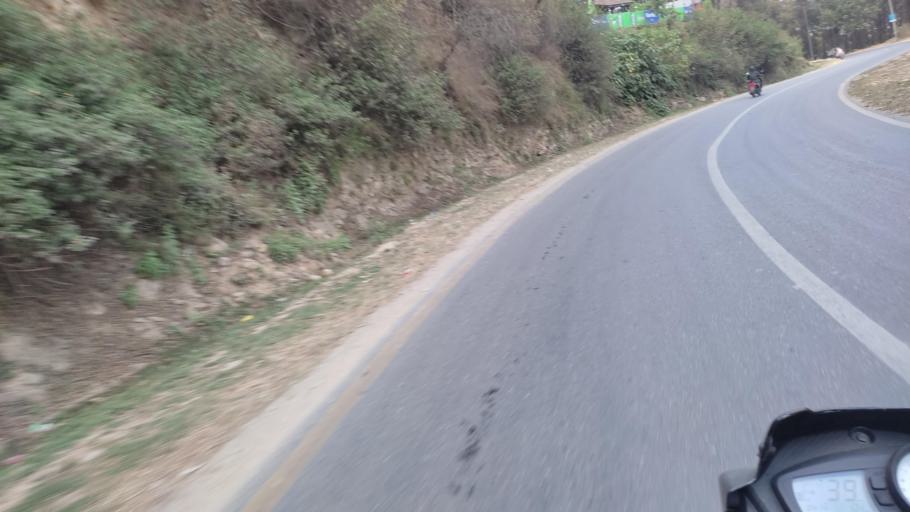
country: NP
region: Central Region
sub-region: Bagmati Zone
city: Patan
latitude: 27.6652
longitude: 85.2947
